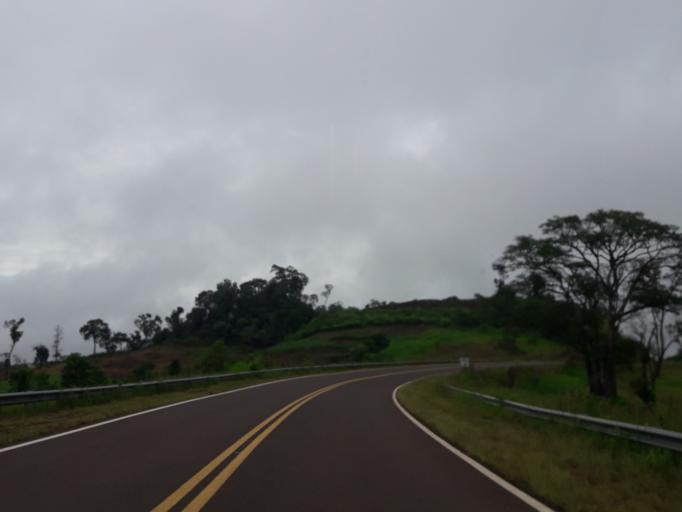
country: AR
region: Misiones
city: Bernardo de Irigoyen
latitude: -26.3981
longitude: -53.8163
